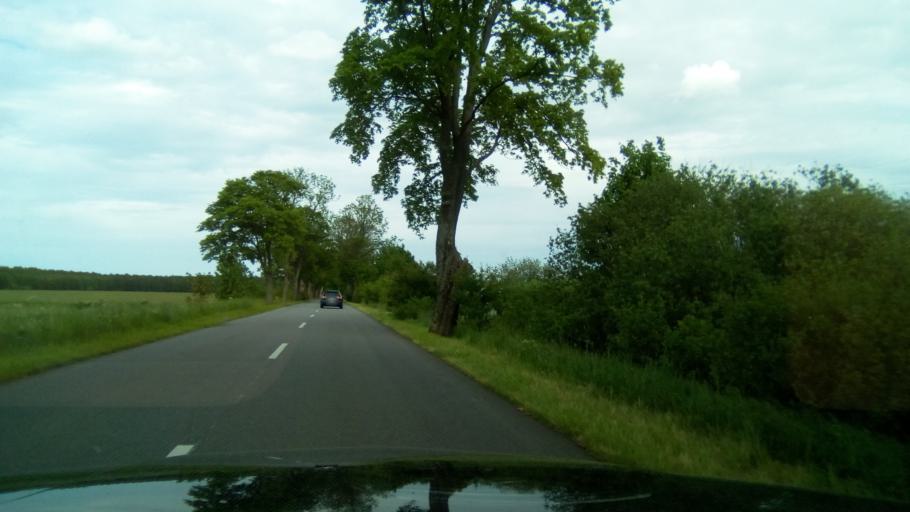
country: PL
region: Pomeranian Voivodeship
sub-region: Powiat pucki
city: Wierzchucino
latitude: 54.7923
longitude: 18.0237
